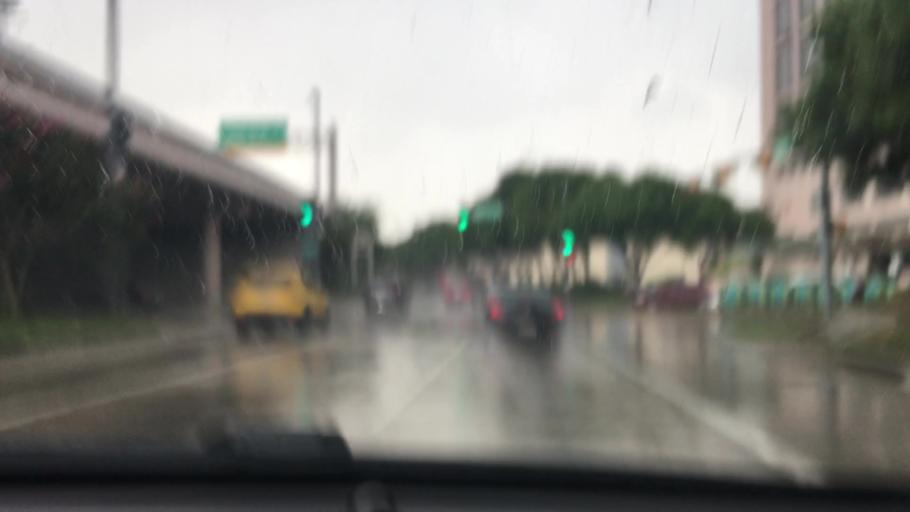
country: US
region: Texas
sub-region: Dallas County
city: Addison
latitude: 32.9291
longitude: -96.8210
